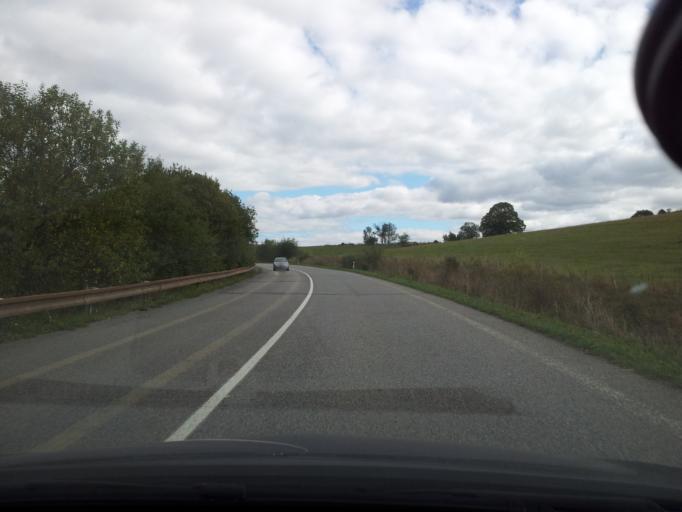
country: SK
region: Zilinsky
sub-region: Okres Liptovsky Mikulas
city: Liptovsky Mikulas
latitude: 49.0556
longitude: 19.4697
